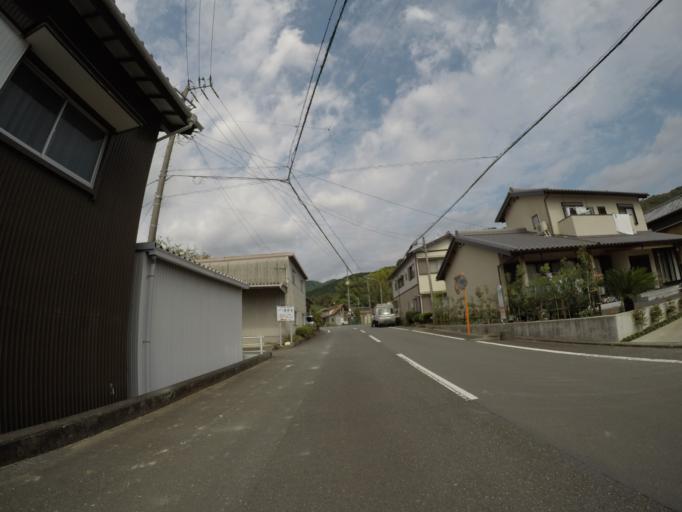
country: JP
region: Shizuoka
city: Shimada
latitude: 34.8661
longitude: 138.1833
